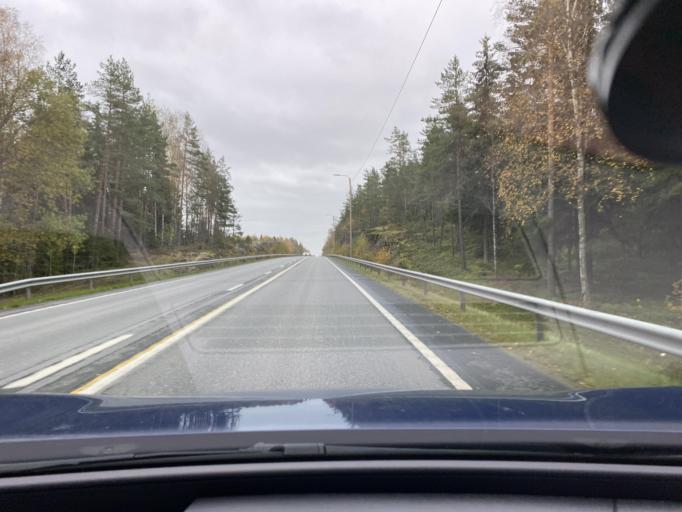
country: FI
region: Varsinais-Suomi
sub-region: Vakka-Suomi
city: Laitila
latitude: 60.9320
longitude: 21.6080
